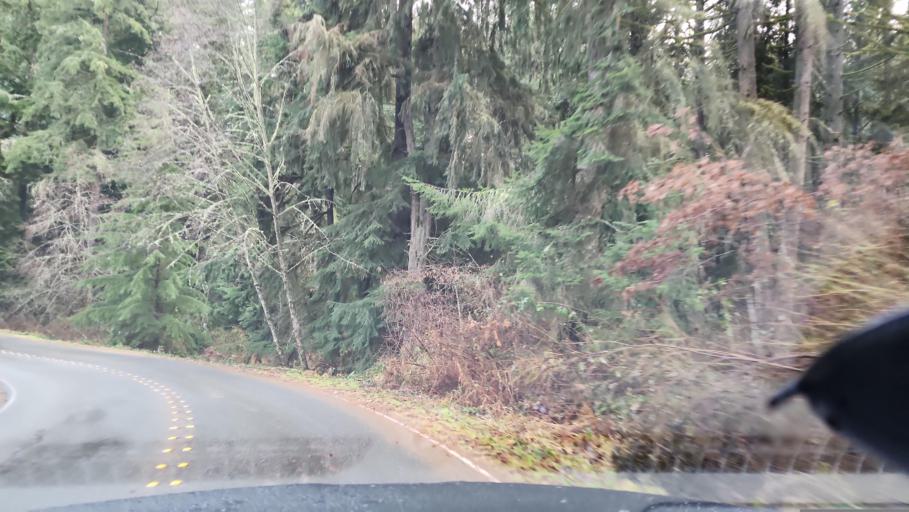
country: US
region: Washington
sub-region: King County
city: Union Hill-Novelty Hill
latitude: 47.6954
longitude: -122.0508
